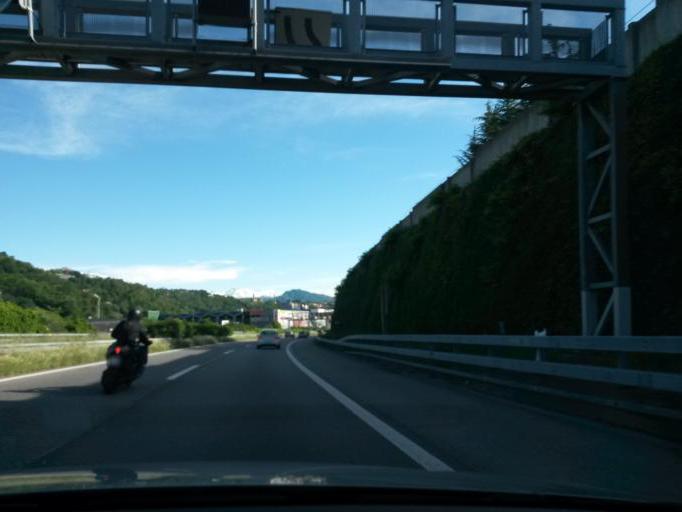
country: CH
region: Ticino
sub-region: Lugano District
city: Montagnola
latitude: 45.9674
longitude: 8.9256
